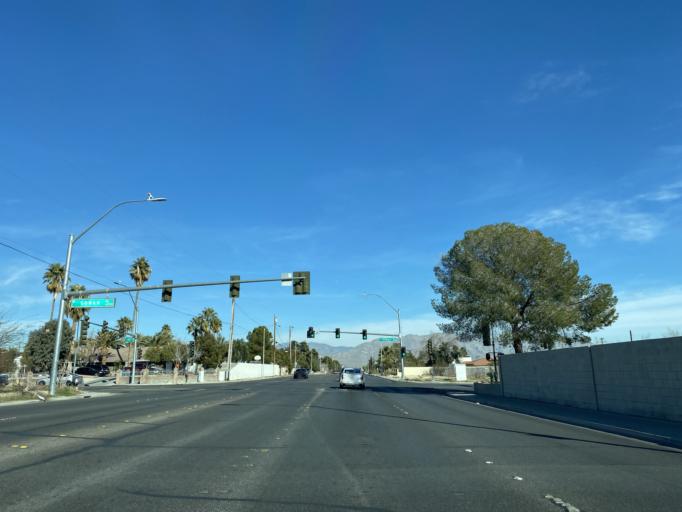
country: US
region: Nevada
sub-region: Clark County
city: Las Vegas
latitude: 36.2238
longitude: -115.2257
